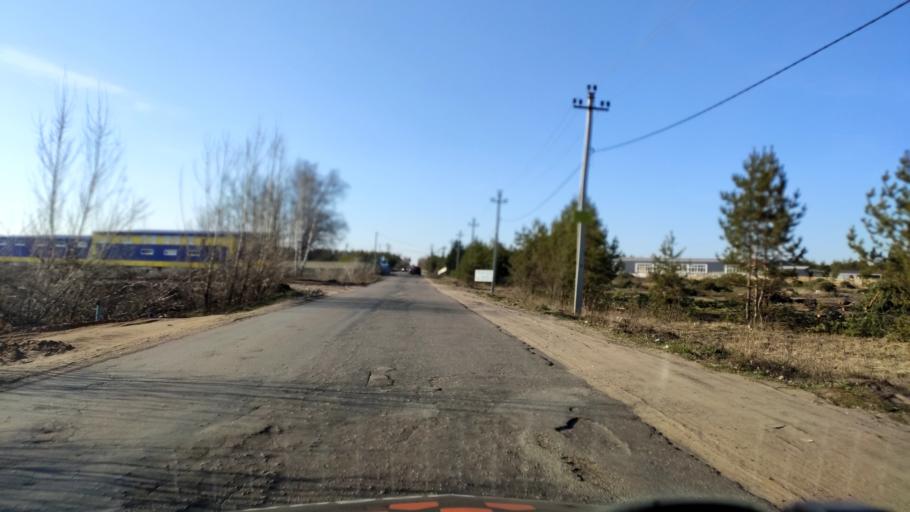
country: RU
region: Voronezj
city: Podgornoye
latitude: 51.8301
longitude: 39.2063
